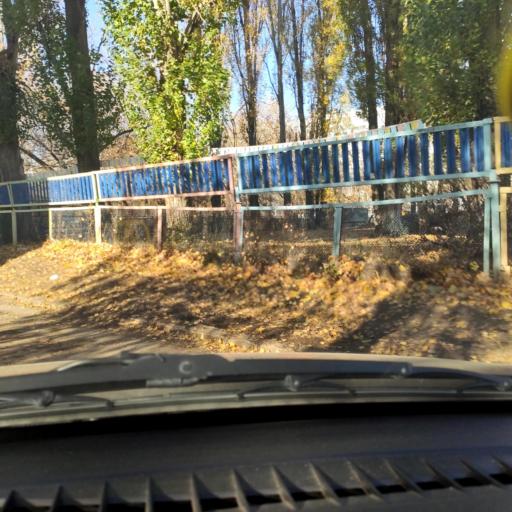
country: RU
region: Samara
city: Tol'yatti
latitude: 53.5352
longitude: 49.2943
